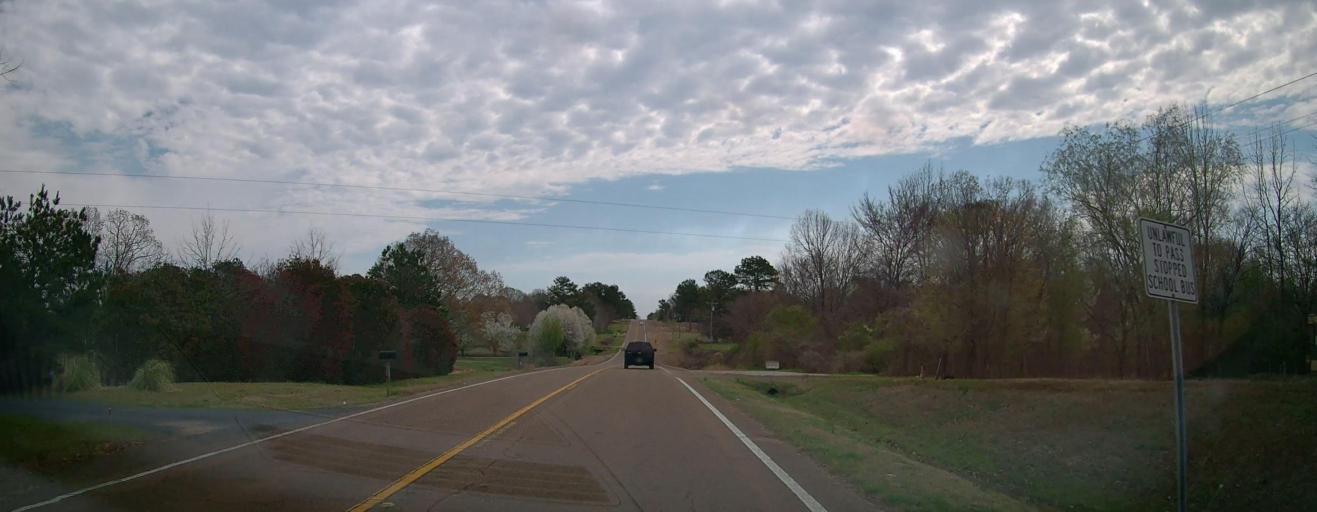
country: US
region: Mississippi
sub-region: Marshall County
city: Byhalia
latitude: 34.8422
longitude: -89.6060
